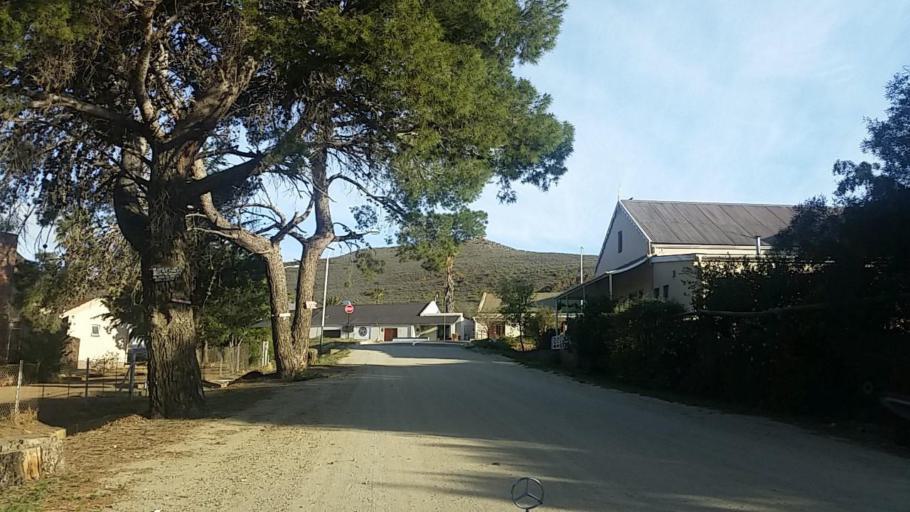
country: ZA
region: Western Cape
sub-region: Eden District Municipality
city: Knysna
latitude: -33.6542
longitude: 23.1301
